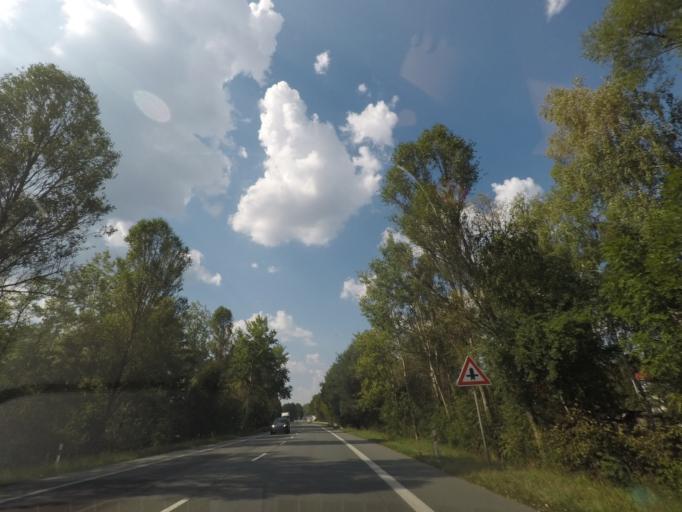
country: CZ
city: Tyniste nad Orlici
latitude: 50.1537
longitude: 16.0675
